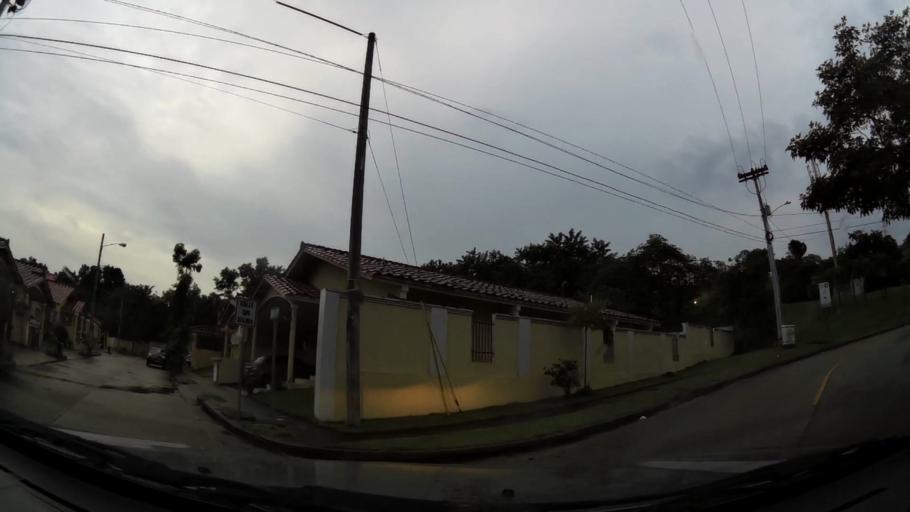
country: PA
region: Panama
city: Las Cumbres
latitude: 9.0412
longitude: -79.5304
